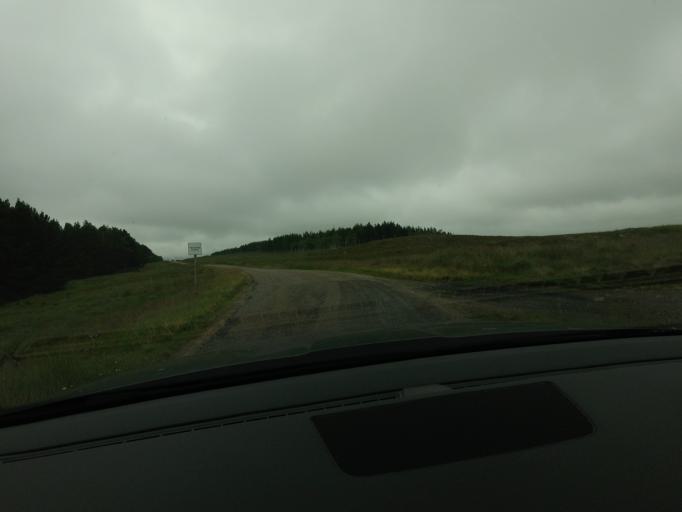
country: GB
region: Scotland
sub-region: Highland
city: Golspie
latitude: 58.3362
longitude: -4.4357
